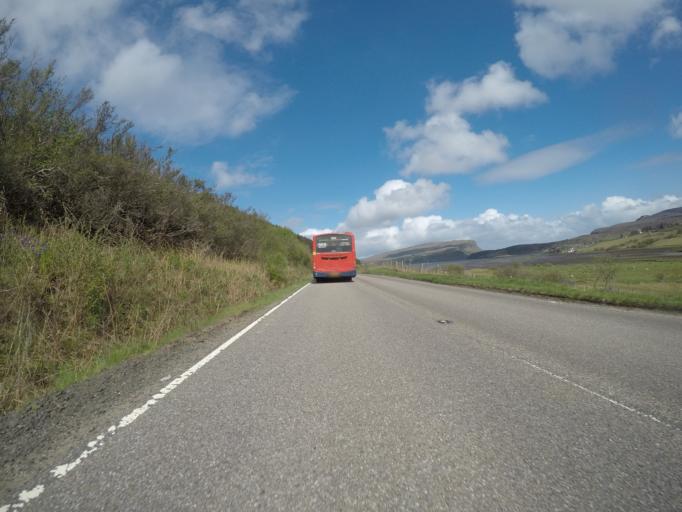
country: GB
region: Scotland
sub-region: Highland
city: Portree
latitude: 57.3909
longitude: -6.2052
